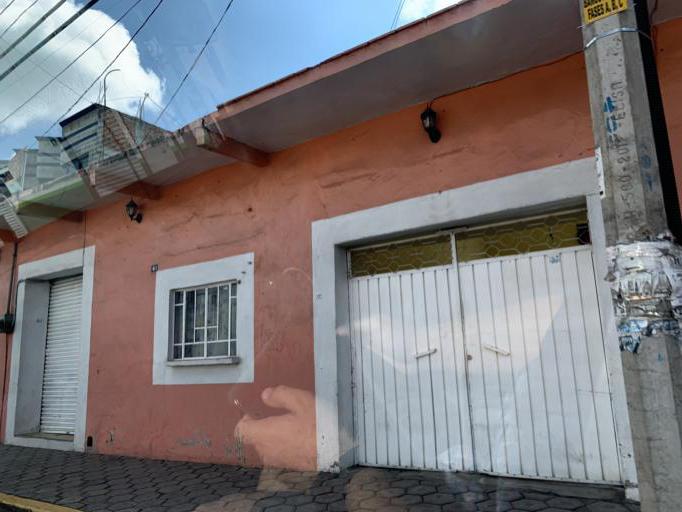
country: MX
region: Puebla
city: Huejotzingo
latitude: 19.1563
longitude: -98.4066
